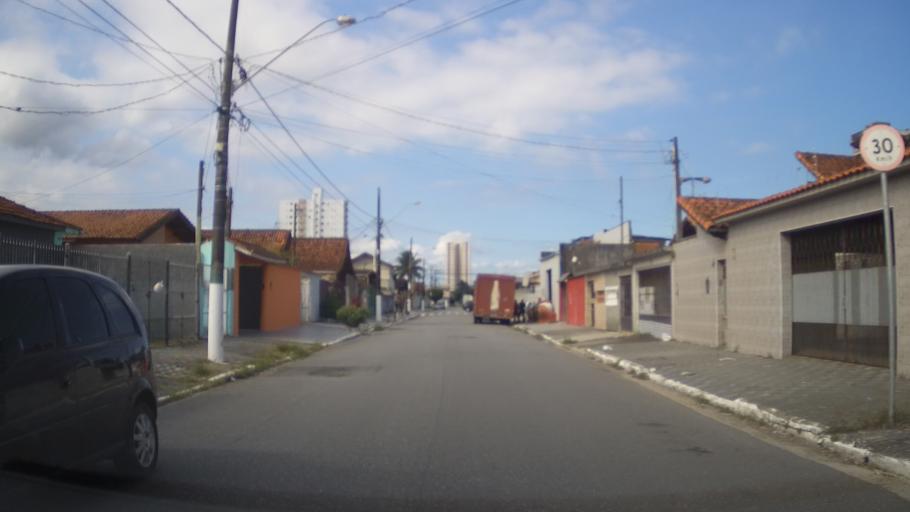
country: BR
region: Sao Paulo
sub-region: Praia Grande
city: Praia Grande
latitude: -24.0187
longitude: -46.4618
